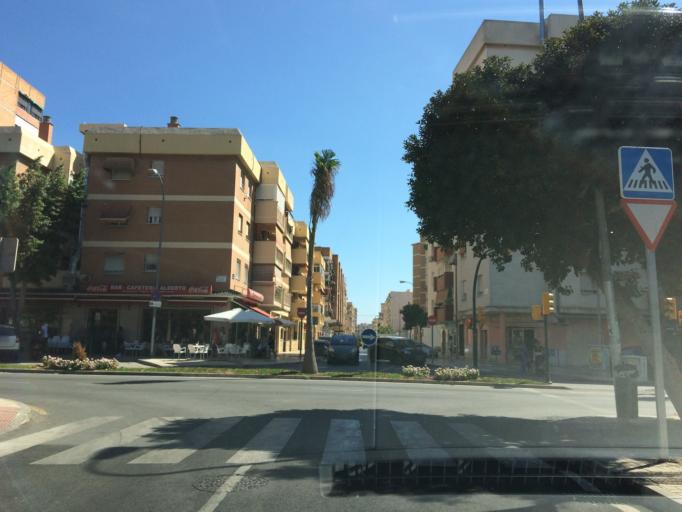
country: ES
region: Andalusia
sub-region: Provincia de Malaga
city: Malaga
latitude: 36.7092
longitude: -4.4517
